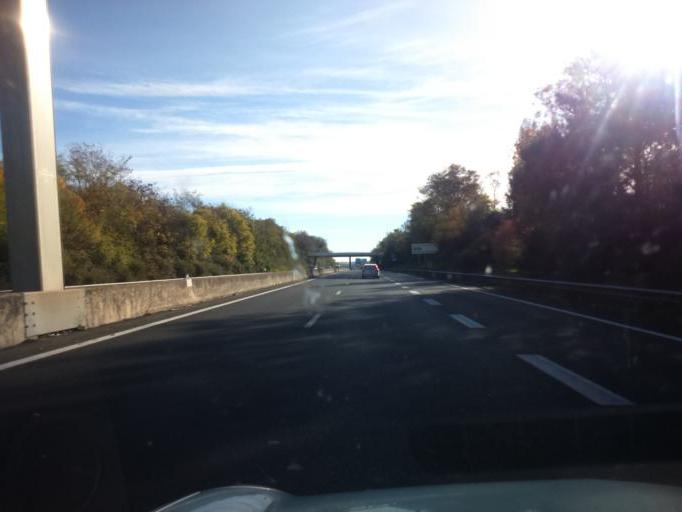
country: FR
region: Poitou-Charentes
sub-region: Departement de la Charente-Maritime
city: Breuil-Magne
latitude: 45.9656
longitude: -0.9732
